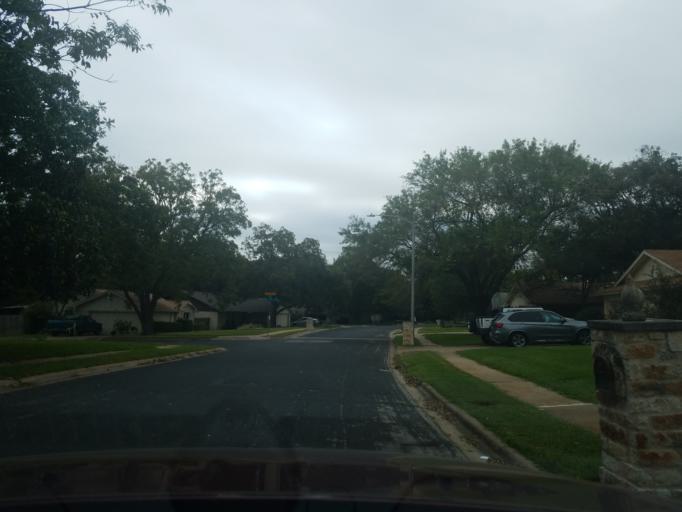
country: US
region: Texas
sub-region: Williamson County
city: Anderson Mill
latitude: 30.4589
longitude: -97.8027
